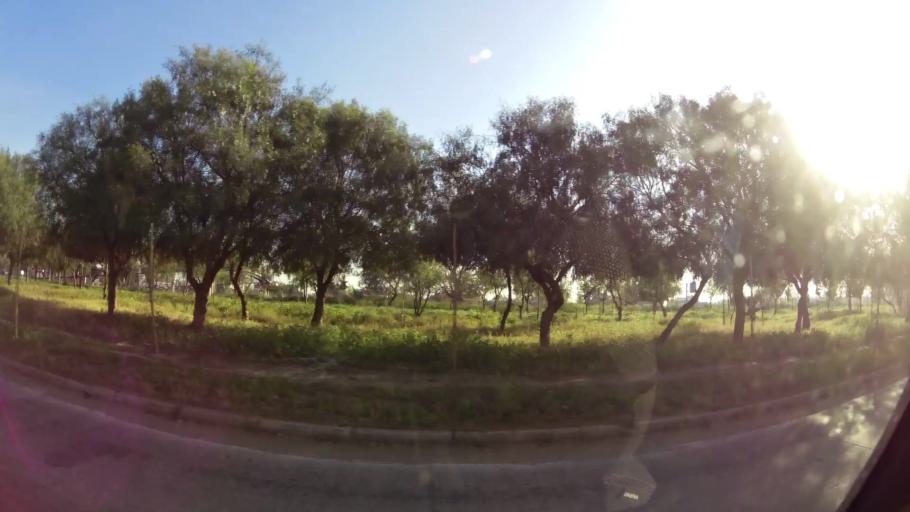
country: CL
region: Santiago Metropolitan
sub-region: Provincia de Santiago
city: Lo Prado
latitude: -33.4515
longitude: -70.7538
